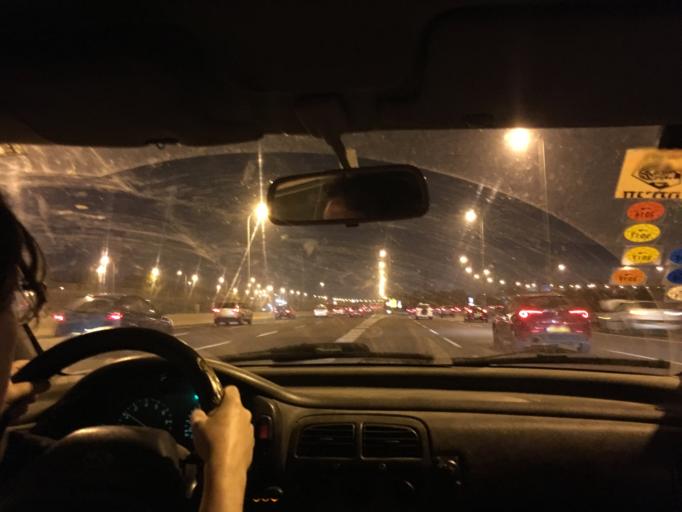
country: IL
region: Tel Aviv
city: Ramat HaSharon
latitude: 32.1328
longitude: 34.8104
